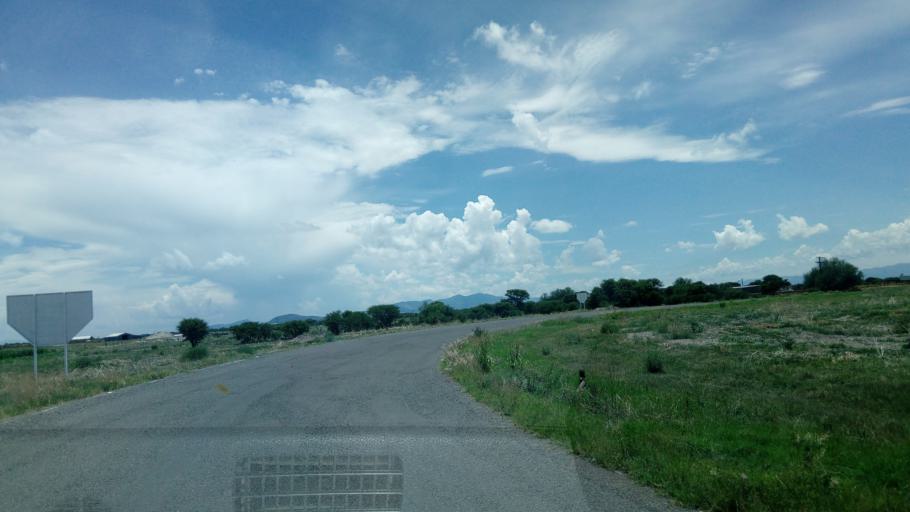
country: MX
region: Durango
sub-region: Durango
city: Jose Refugio Salcido
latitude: 24.1700
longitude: -104.4983
